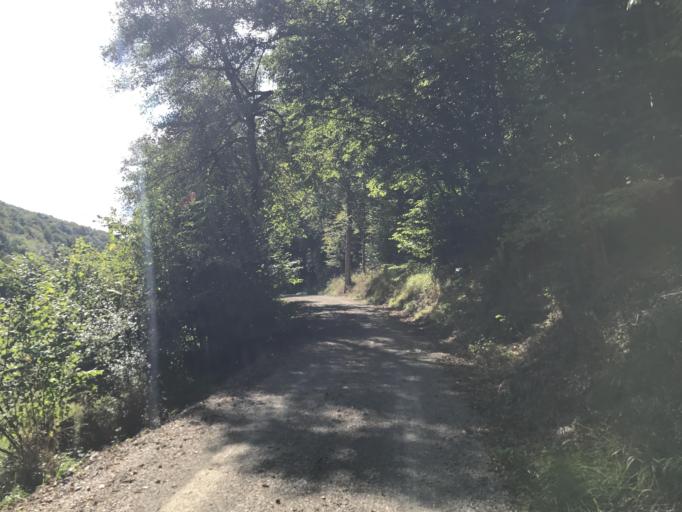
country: DE
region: Hesse
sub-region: Regierungsbezirk Kassel
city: Sachsenhausen
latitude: 51.2223
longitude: 9.0284
